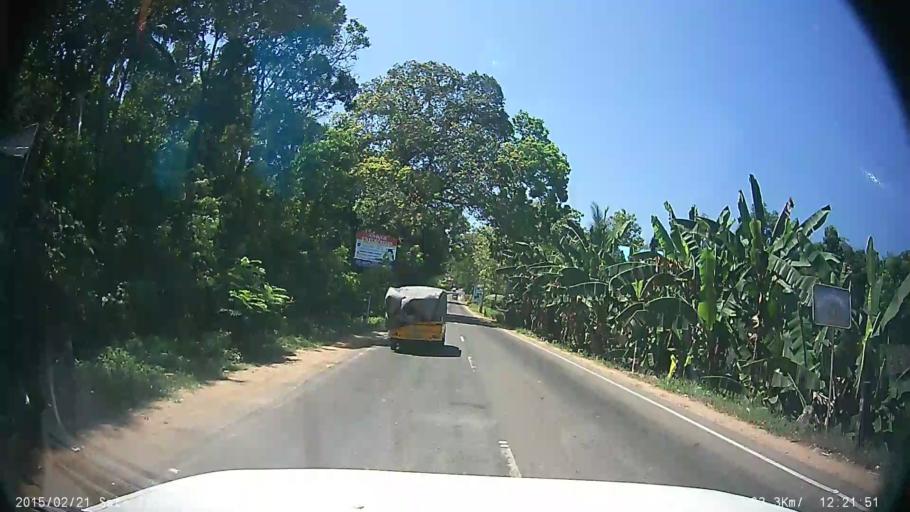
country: IN
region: Kerala
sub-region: Kottayam
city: Palackattumala
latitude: 9.6754
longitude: 76.5985
